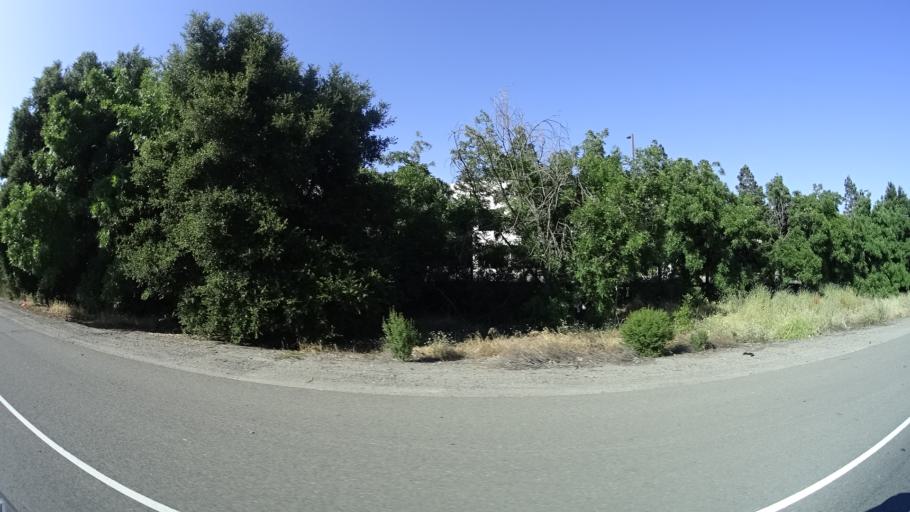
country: US
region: California
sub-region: Santa Clara County
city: Seven Trees
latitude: 37.2496
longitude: -121.7823
